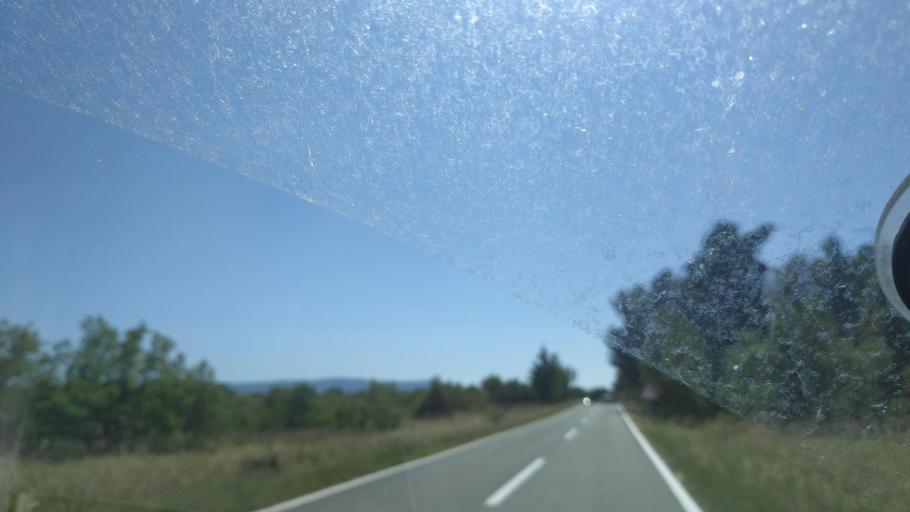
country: HR
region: Sibensko-Kniniska
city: Drnis
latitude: 43.8184
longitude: 16.0602
